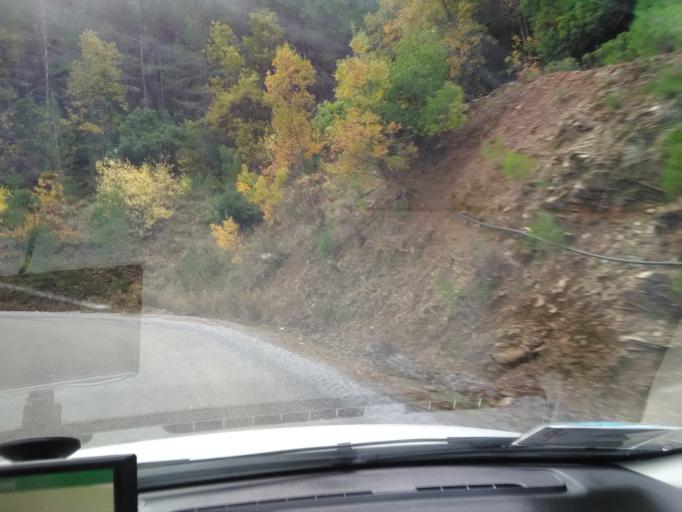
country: TR
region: Antalya
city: Gazipasa
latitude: 36.2462
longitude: 32.4306
